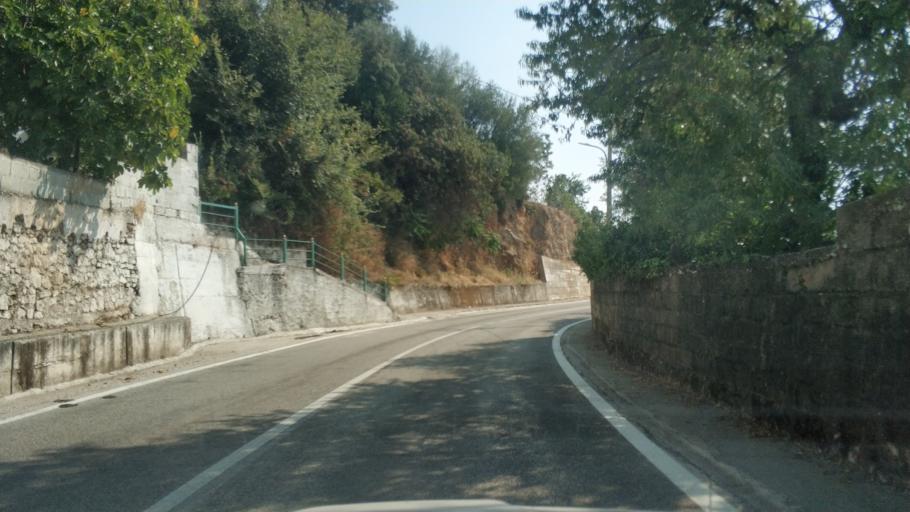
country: AL
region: Vlore
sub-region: Rrethi i Sarandes
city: Lukove
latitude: 40.0187
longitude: 19.8920
